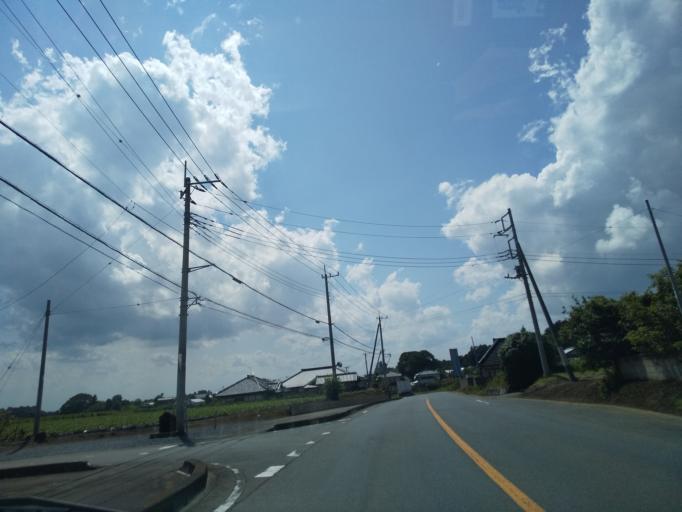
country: JP
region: Ibaraki
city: Okunoya
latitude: 36.1613
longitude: 140.3907
